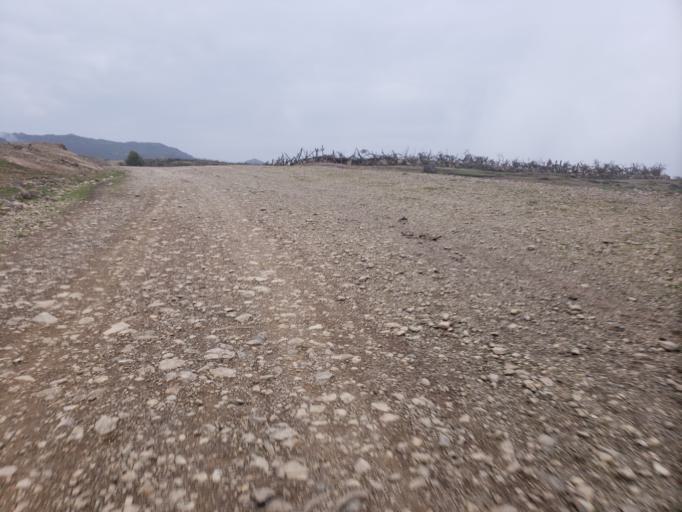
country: ET
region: Oromiya
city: Dodola
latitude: 6.7291
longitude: 39.4289
